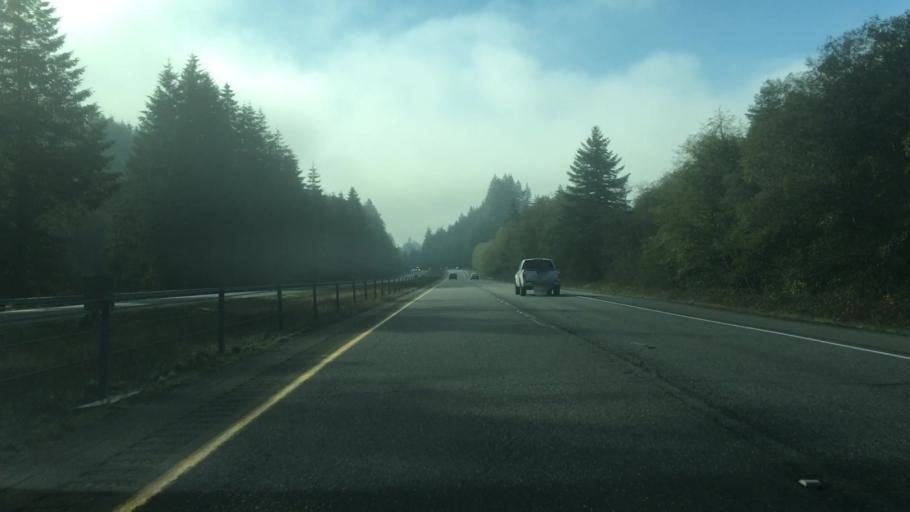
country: US
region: Washington
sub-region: Grays Harbor County
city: McCleary
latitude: 47.0403
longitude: -123.3244
